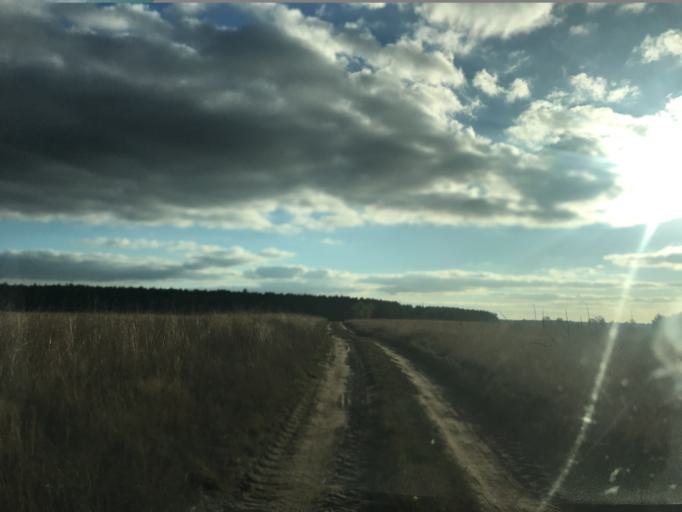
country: PL
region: Warmian-Masurian Voivodeship
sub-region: Powiat dzialdowski
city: Rybno
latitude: 53.3707
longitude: 19.8274
